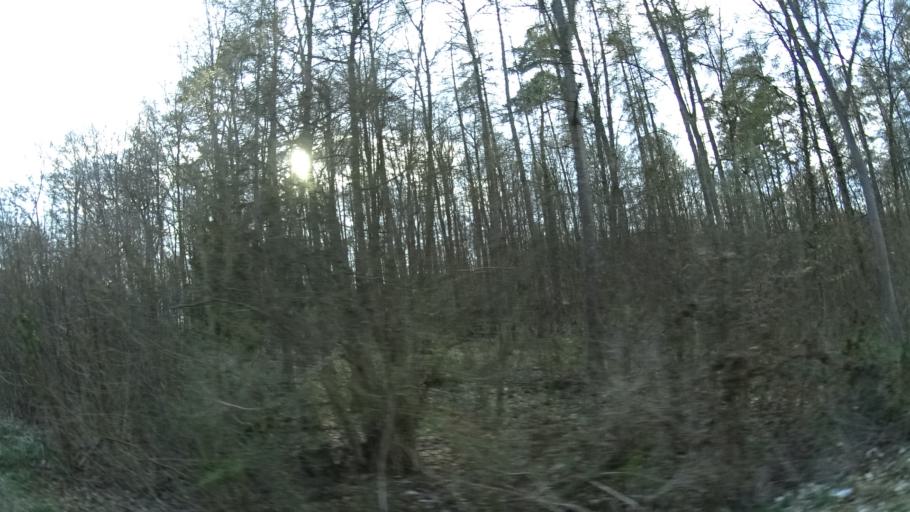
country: DE
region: Rheinland-Pfalz
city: Lauschied
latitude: 49.7519
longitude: 7.6154
